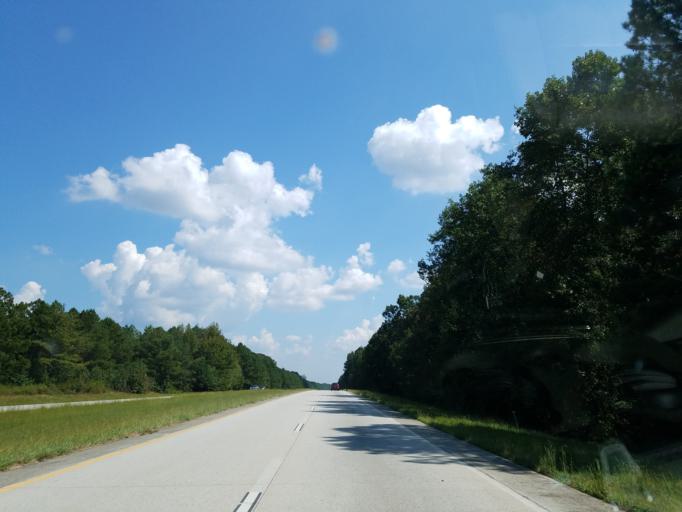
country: US
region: Georgia
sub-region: Oconee County
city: Bogart
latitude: 33.9385
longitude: -83.5497
